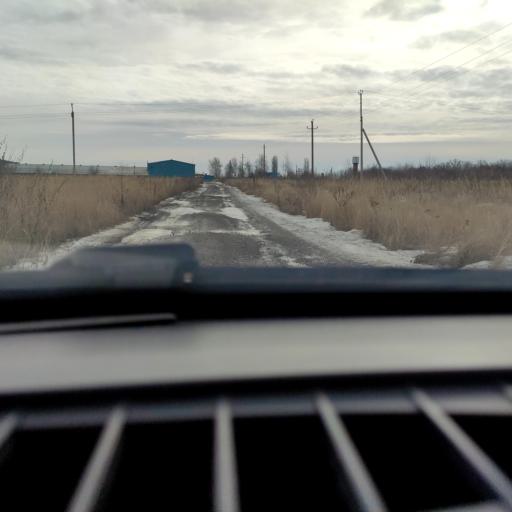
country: RU
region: Voronezj
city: Semiluki
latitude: 51.7312
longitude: 38.9809
